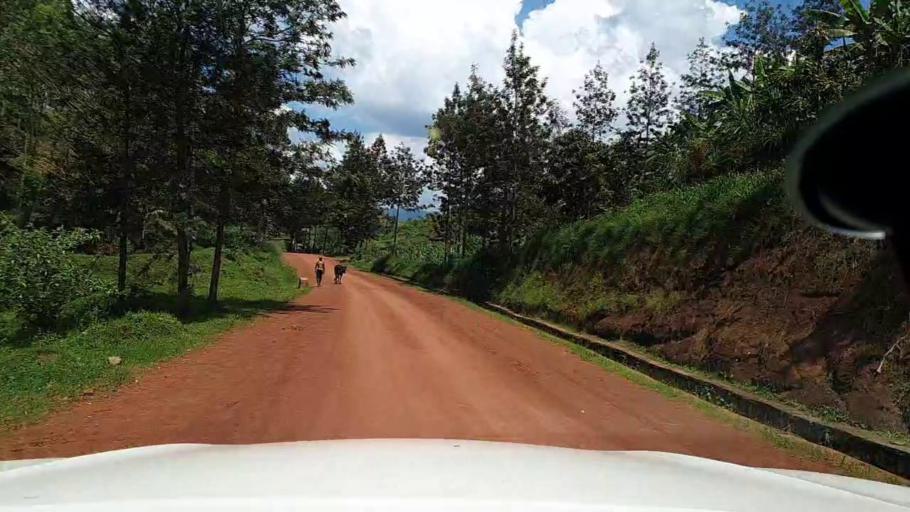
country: RW
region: Northern Province
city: Byumba
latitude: -1.7018
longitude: 29.8363
